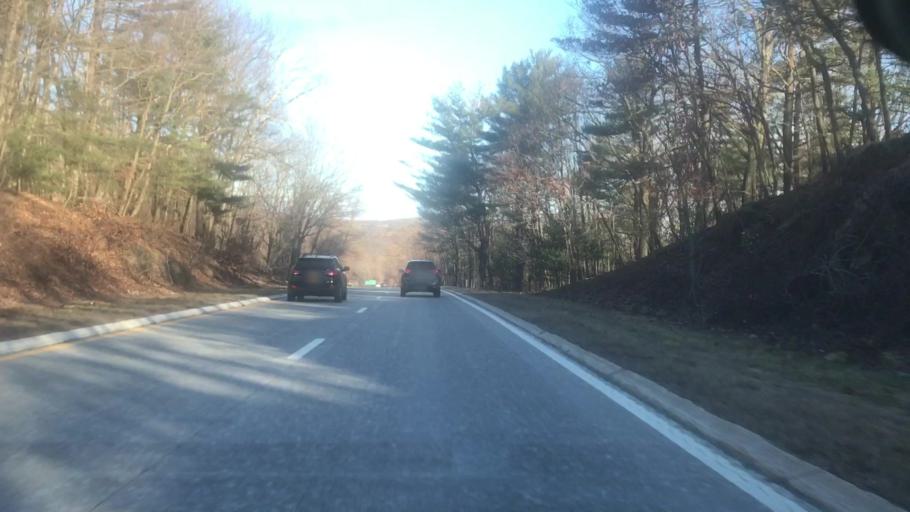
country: US
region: New York
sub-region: Rockland County
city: Thiells
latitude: 41.2119
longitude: -74.0323
